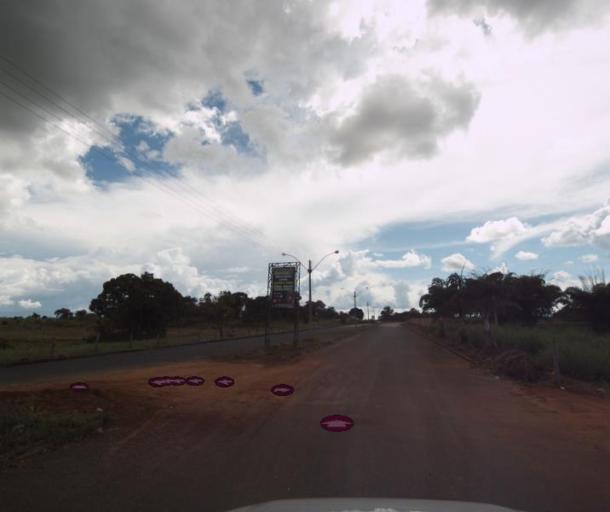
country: BR
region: Goias
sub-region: Porangatu
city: Porangatu
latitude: -13.4832
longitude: -49.1370
